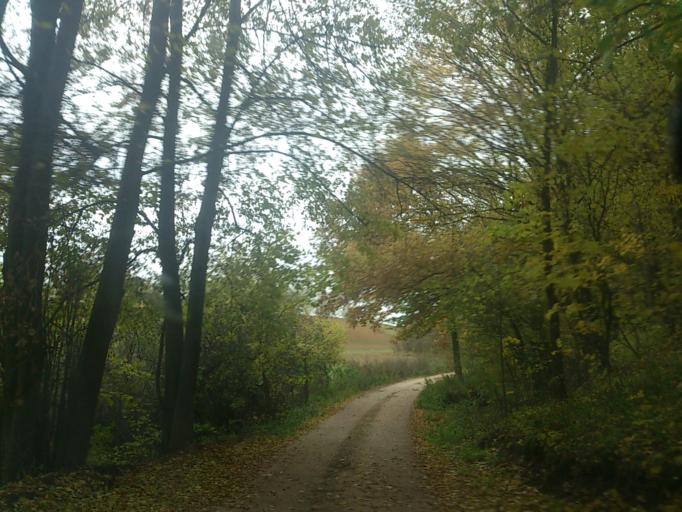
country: PL
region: Kujawsko-Pomorskie
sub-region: Powiat golubsko-dobrzynski
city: Golub-Dobrzyn
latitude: 53.1241
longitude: 19.0627
